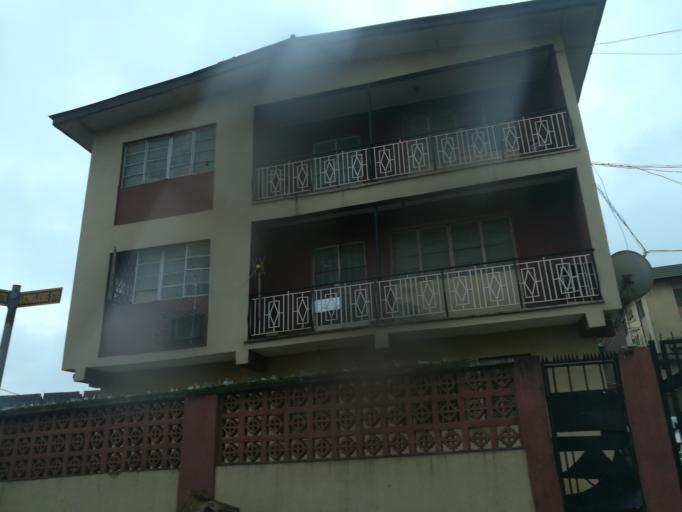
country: NG
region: Lagos
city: Oshodi
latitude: 6.5669
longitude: 3.3414
